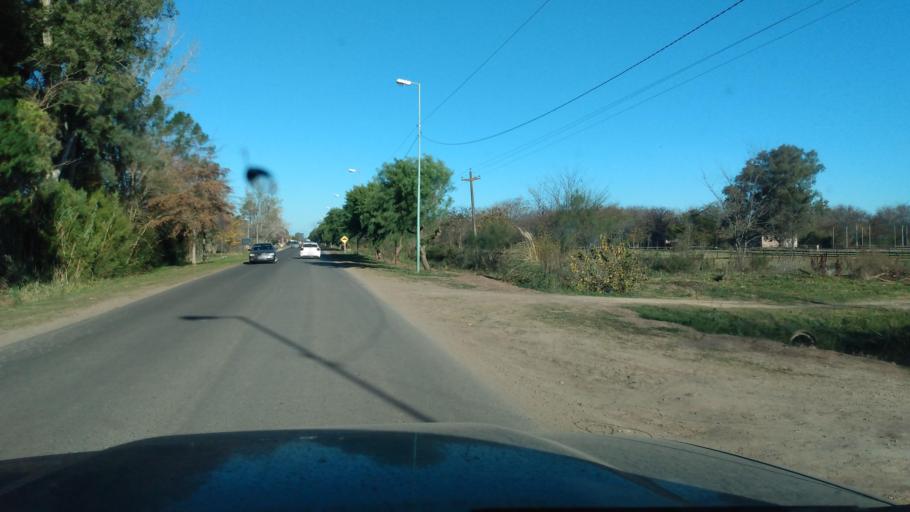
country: AR
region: Buenos Aires
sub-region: Partido de Lujan
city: Lujan
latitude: -34.4847
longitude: -59.2158
